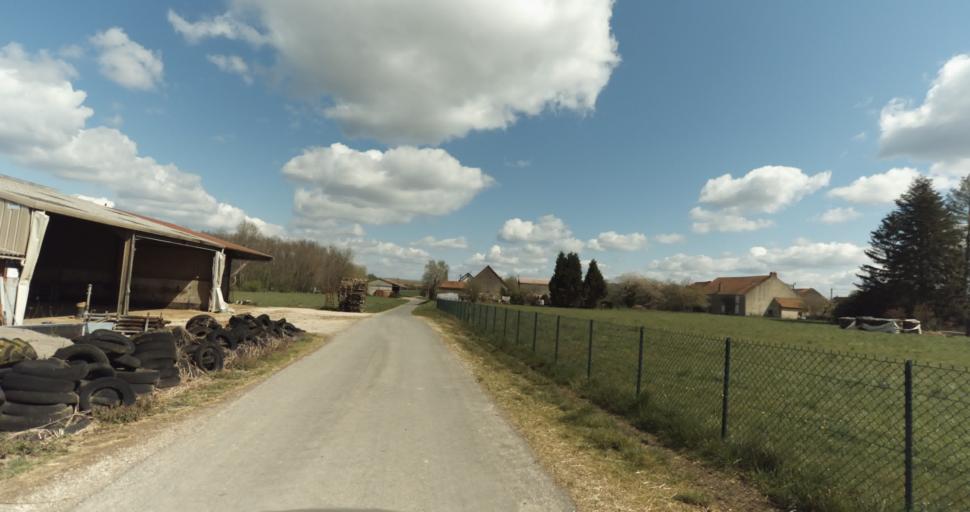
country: FR
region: Bourgogne
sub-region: Departement de la Cote-d'Or
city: Auxonne
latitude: 47.2095
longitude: 5.4107
